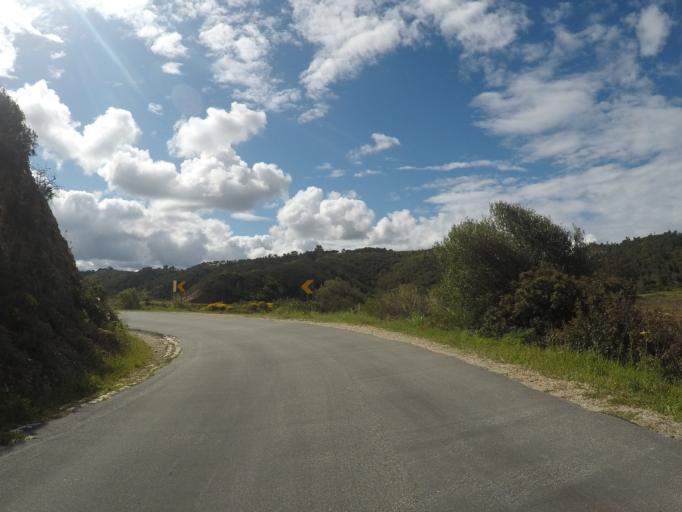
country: PT
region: Beja
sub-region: Odemira
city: Sao Teotonio
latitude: 37.4361
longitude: -8.7869
